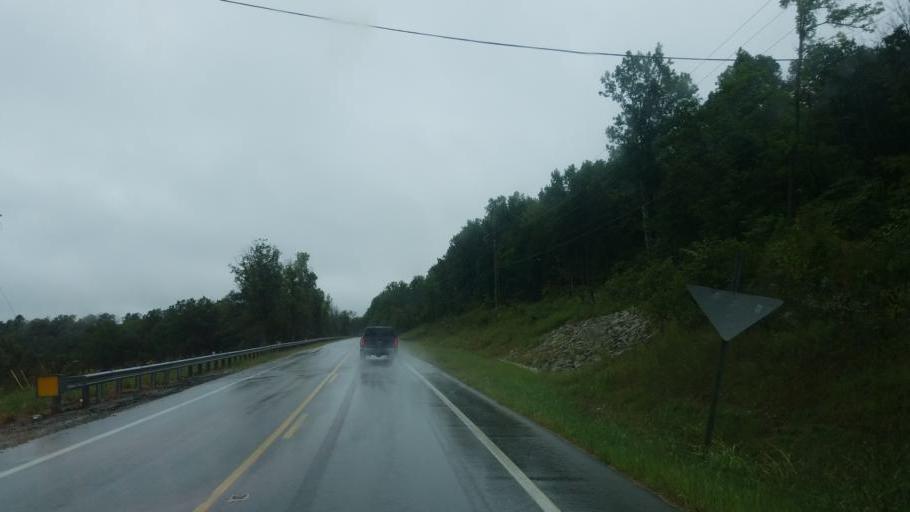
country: US
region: Ohio
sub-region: Adams County
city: West Union
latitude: 38.7930
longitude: -83.4650
